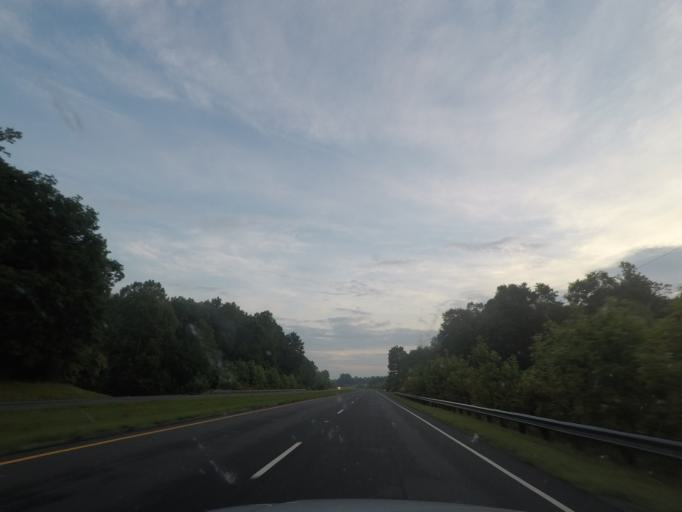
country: US
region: North Carolina
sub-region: Person County
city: Roxboro
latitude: 36.3079
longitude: -78.9709
